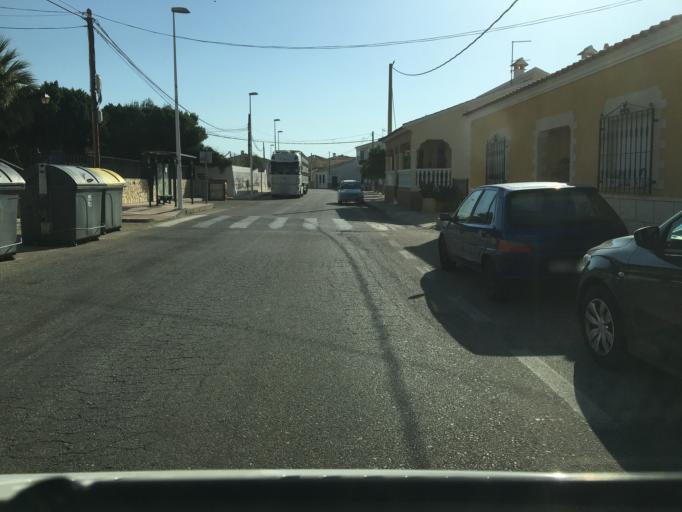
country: ES
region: Andalusia
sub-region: Provincia de Almeria
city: Huercal-Overa
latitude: 37.4673
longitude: -1.9199
